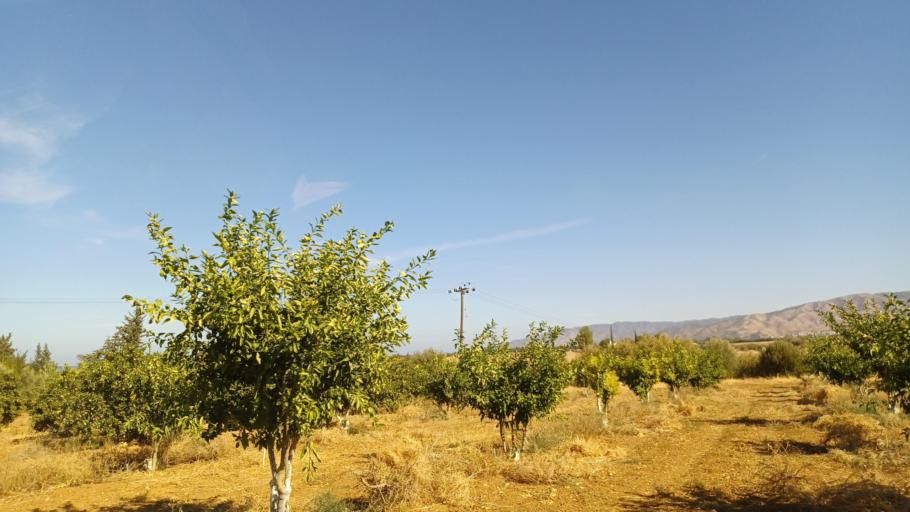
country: CY
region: Pafos
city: Polis
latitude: 35.0413
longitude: 32.4410
